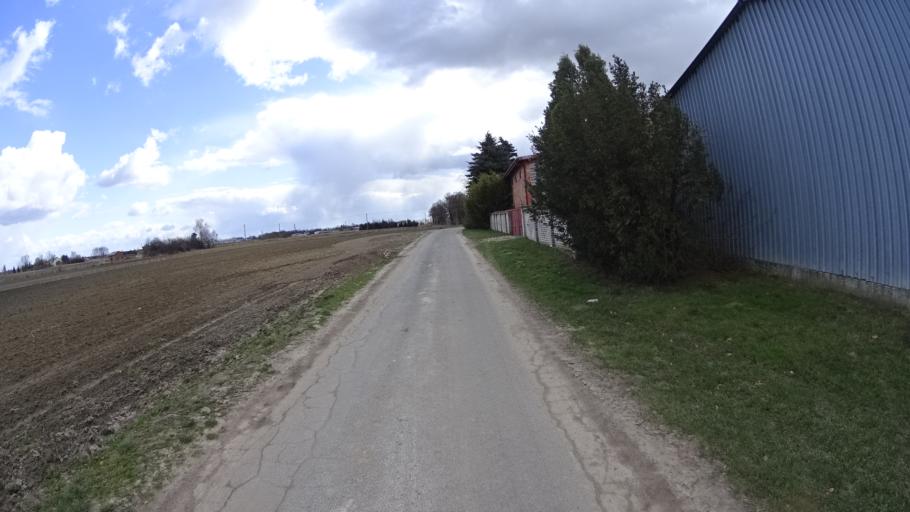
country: PL
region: Masovian Voivodeship
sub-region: Powiat warszawski zachodni
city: Jozefow
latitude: 52.2215
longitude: 20.6771
